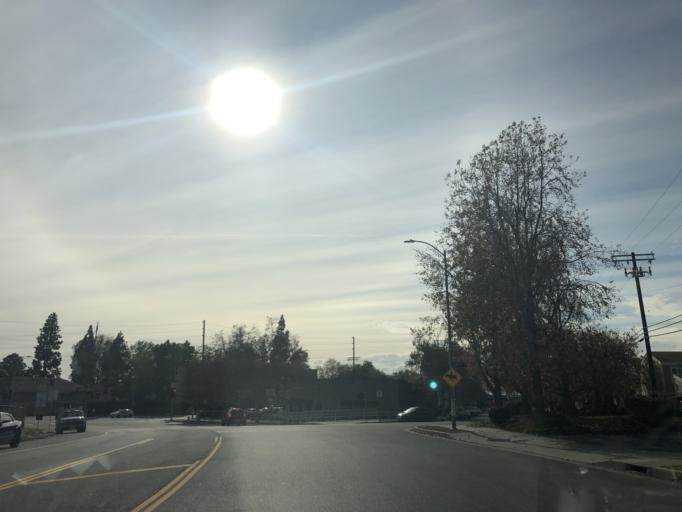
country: US
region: California
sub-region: Los Angeles County
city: San Fernando
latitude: 34.2772
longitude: -118.3780
